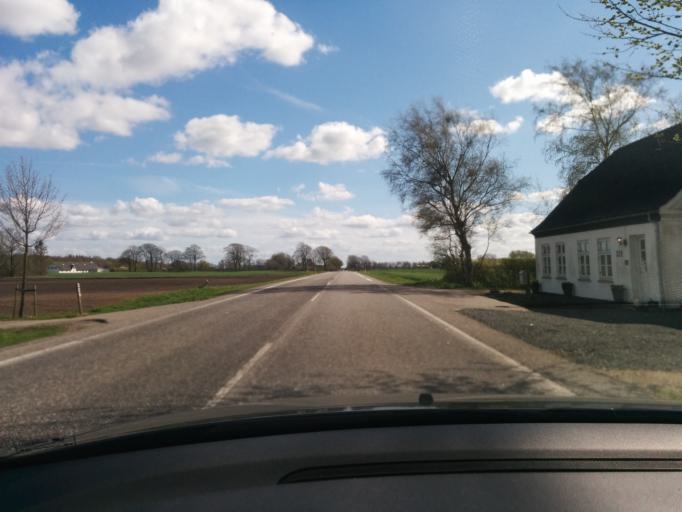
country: DK
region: South Denmark
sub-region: Kolding Kommune
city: Christiansfeld
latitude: 55.4234
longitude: 9.4764
